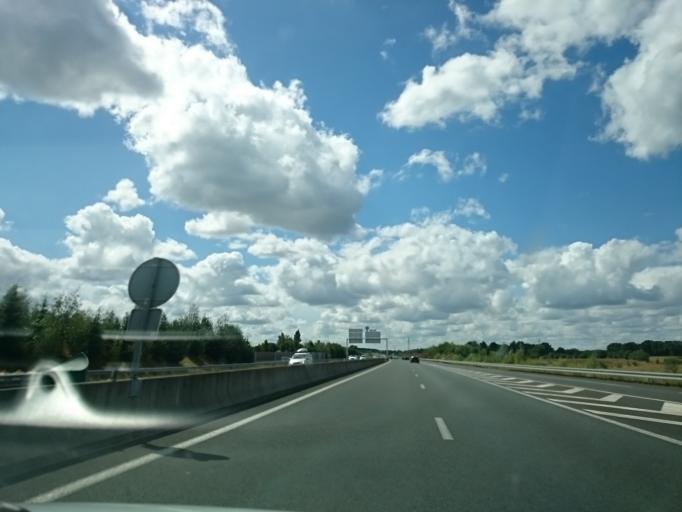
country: FR
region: Pays de la Loire
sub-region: Departement de Maine-et-Loire
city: Beaucouze
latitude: 47.4939
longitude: -0.6264
